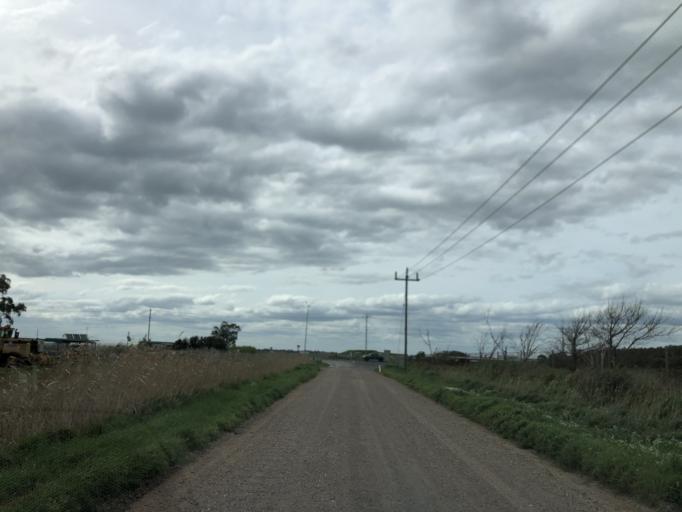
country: AU
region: Victoria
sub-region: Kingston
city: Patterson Lakes
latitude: -38.0699
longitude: 145.1668
